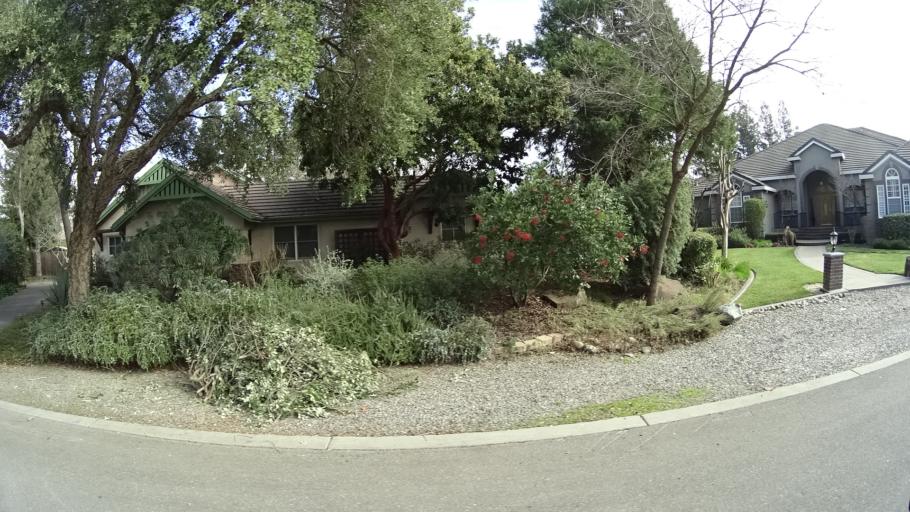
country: US
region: California
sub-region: Yolo County
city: Davis
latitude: 38.5374
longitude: -121.7185
